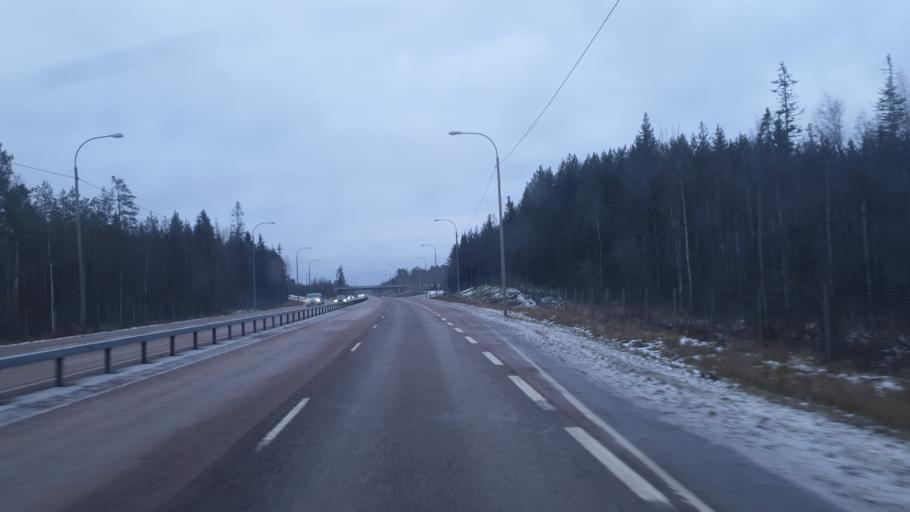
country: FI
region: Northern Savo
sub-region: Varkaus
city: Varkaus
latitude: 62.2647
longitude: 27.8672
